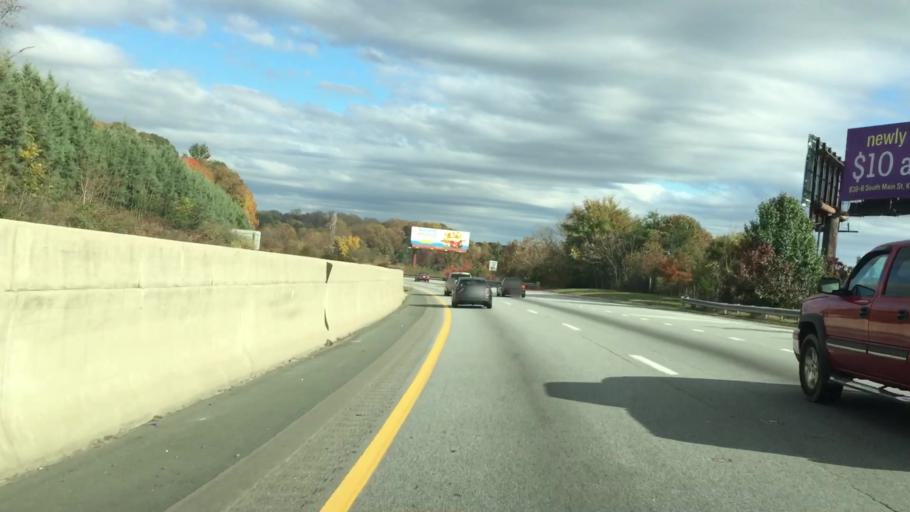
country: US
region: North Carolina
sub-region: Forsyth County
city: Winston-Salem
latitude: 36.0941
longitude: -80.2229
